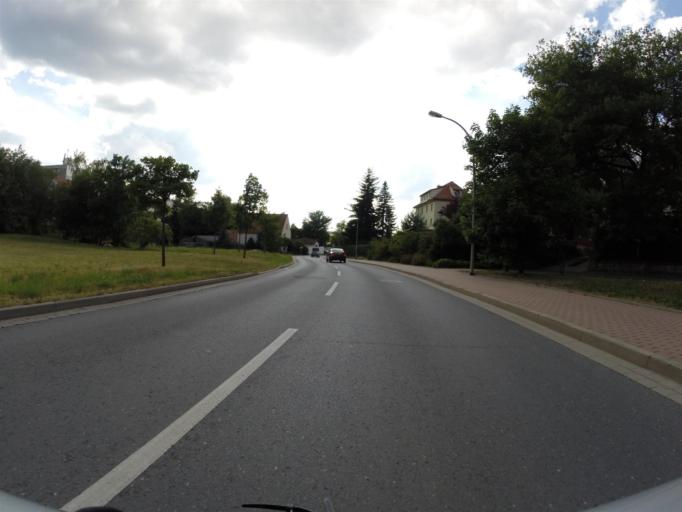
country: DE
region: Thuringia
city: Stadtroda
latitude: 50.8634
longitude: 11.7351
